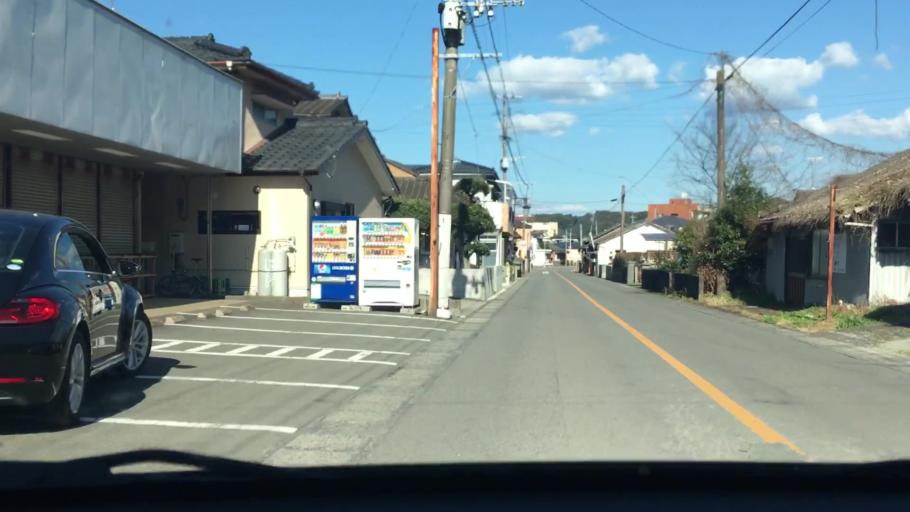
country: JP
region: Kagoshima
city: Satsumasendai
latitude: 31.7865
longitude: 130.4032
